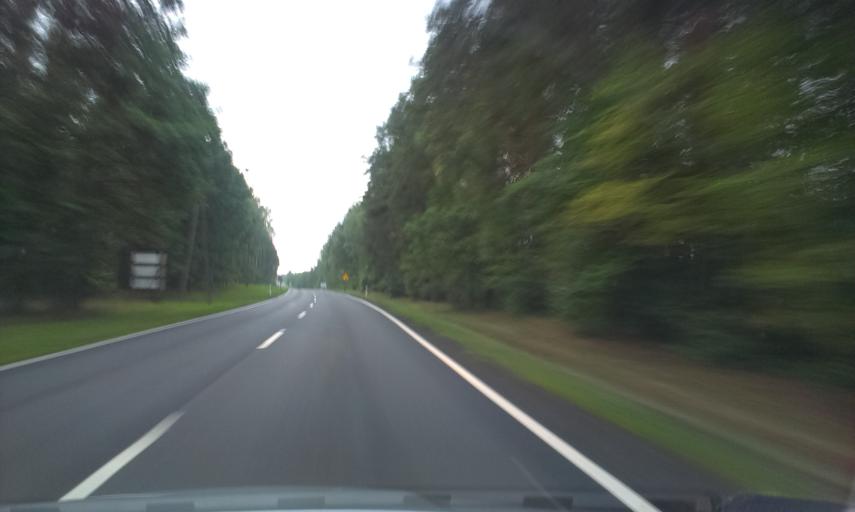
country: PL
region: Greater Poland Voivodeship
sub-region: Powiat zlotowski
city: Tarnowka
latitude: 53.3154
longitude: 16.7944
